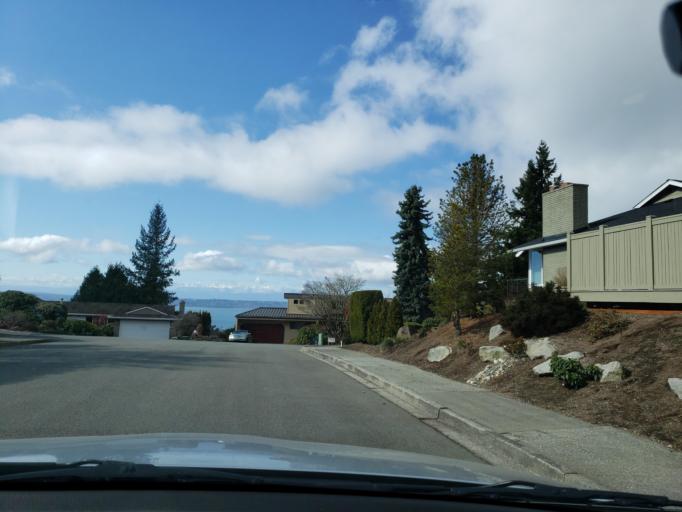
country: US
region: Washington
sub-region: Snohomish County
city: Edmonds
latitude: 47.8147
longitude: -122.3566
